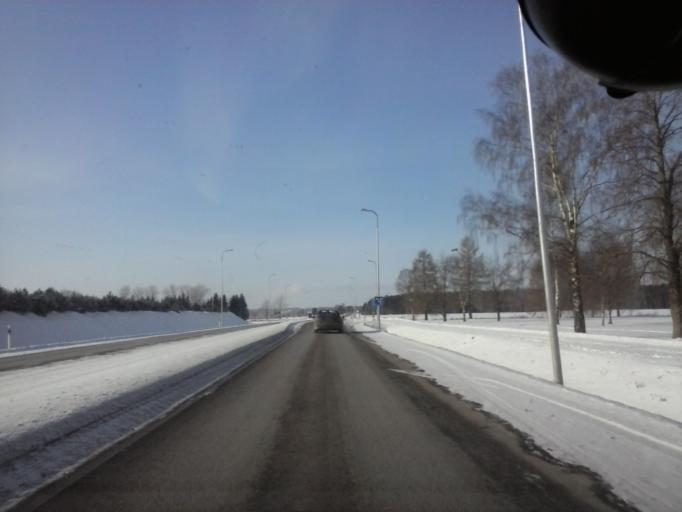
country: EE
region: Tartu
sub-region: Tartu linn
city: Tartu
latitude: 58.3594
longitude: 26.6455
